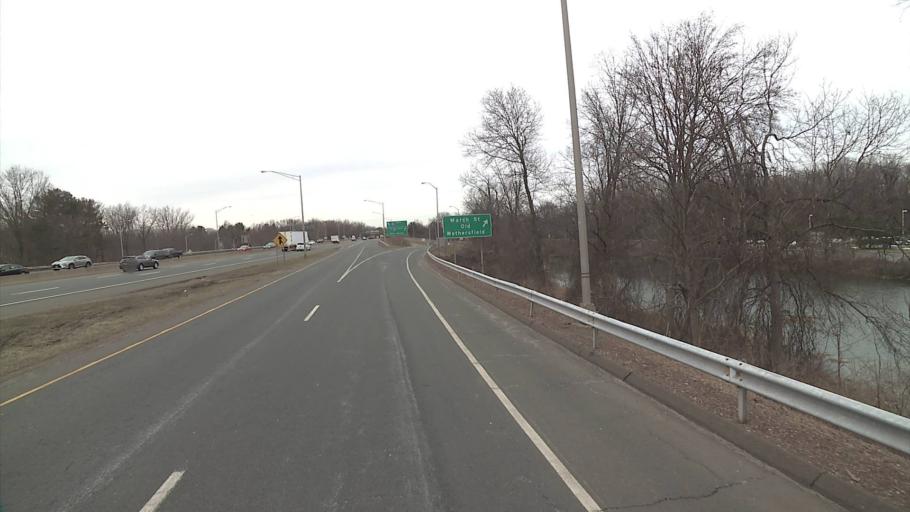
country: US
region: Connecticut
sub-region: Hartford County
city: Wethersfield
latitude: 41.7123
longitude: -72.6467
